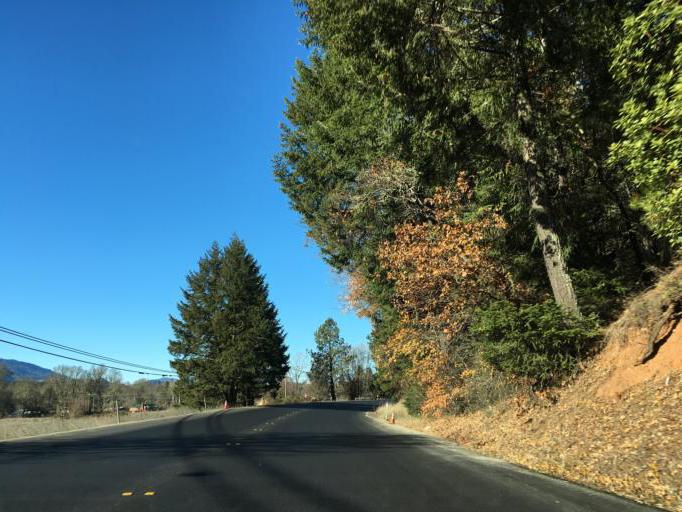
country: US
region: California
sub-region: Mendocino County
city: Laytonville
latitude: 39.6575
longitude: -123.4771
